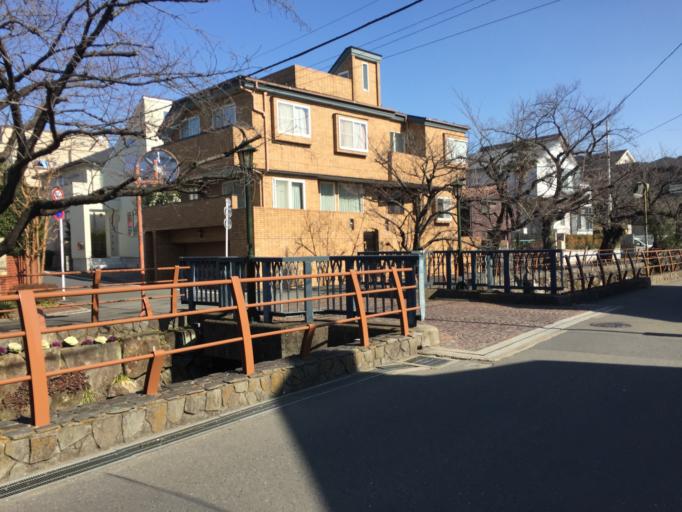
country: JP
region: Kanagawa
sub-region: Kawasaki-shi
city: Kawasaki
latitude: 35.5977
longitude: 139.6557
